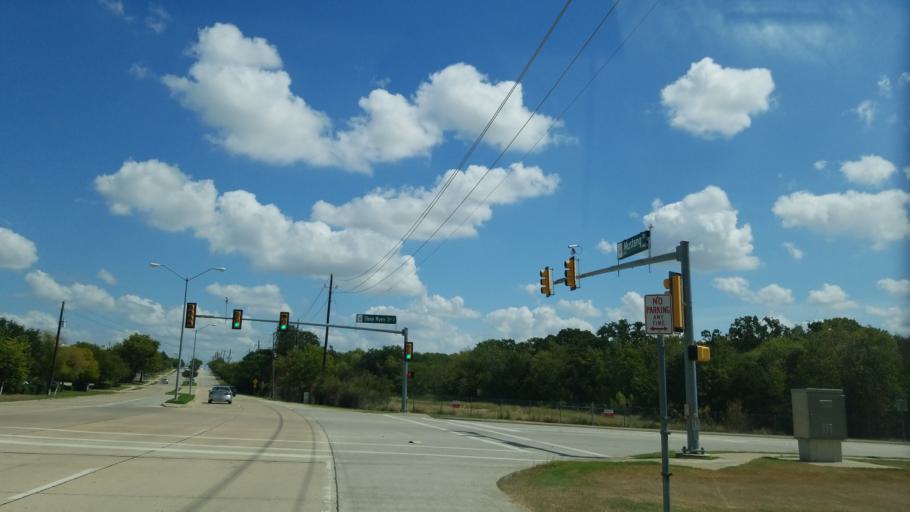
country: US
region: Texas
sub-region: Tarrant County
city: Grapevine
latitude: 32.9182
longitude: -97.0868
